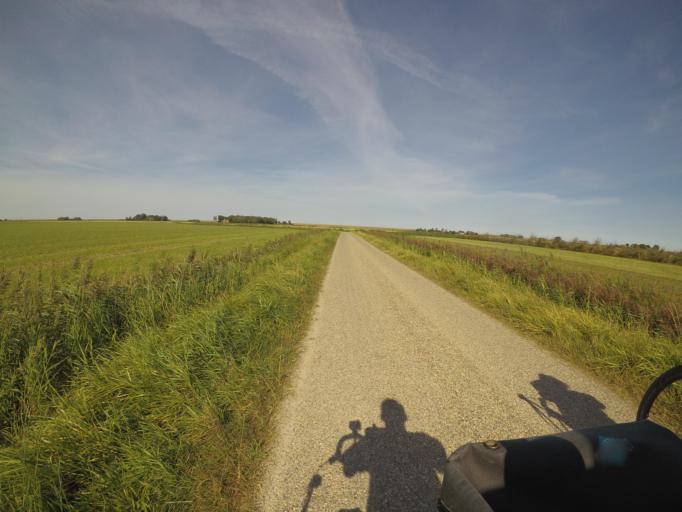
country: NL
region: Friesland
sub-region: Gemeente Ferwerderadiel
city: Ferwert
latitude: 53.3396
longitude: 5.8163
